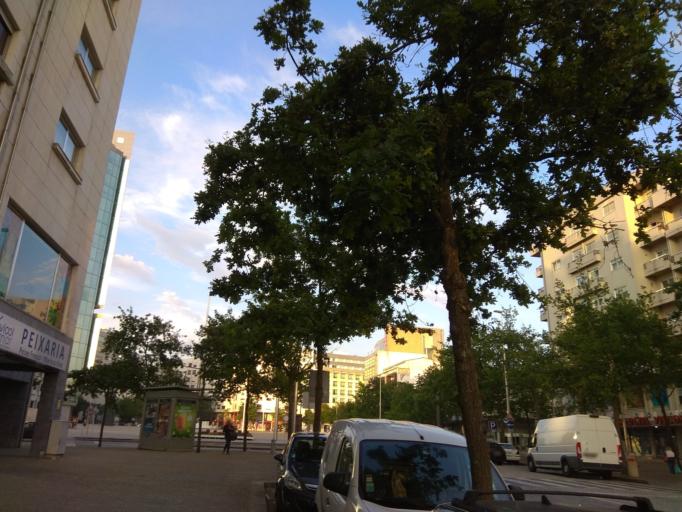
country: PT
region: Porto
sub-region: Maia
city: Maia
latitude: 41.2328
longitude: -8.6237
